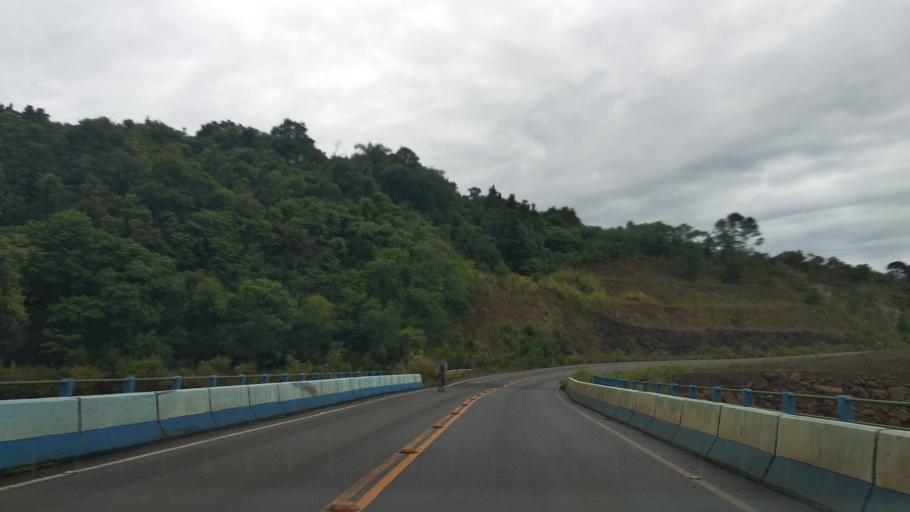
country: BR
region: Santa Catarina
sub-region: Videira
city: Videira
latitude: -27.0030
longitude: -51.1713
